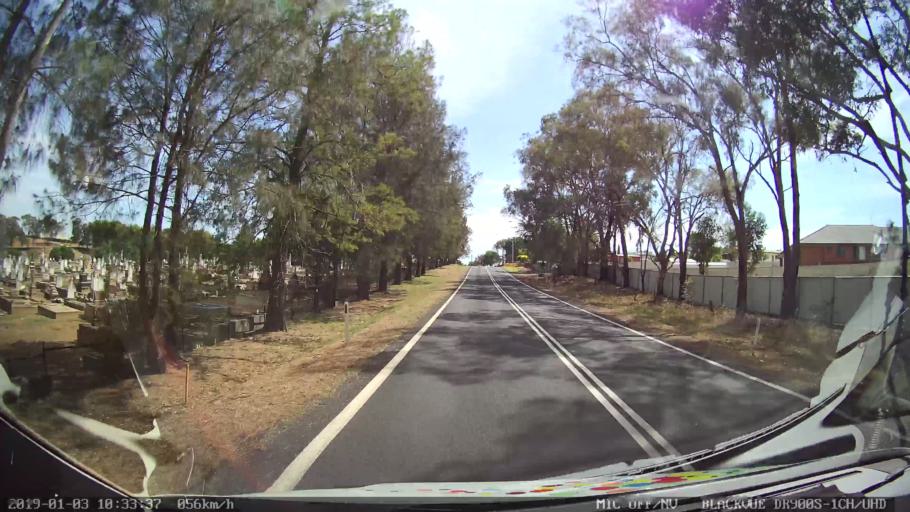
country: AU
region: New South Wales
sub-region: Young
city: Young
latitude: -34.3270
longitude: 148.2887
